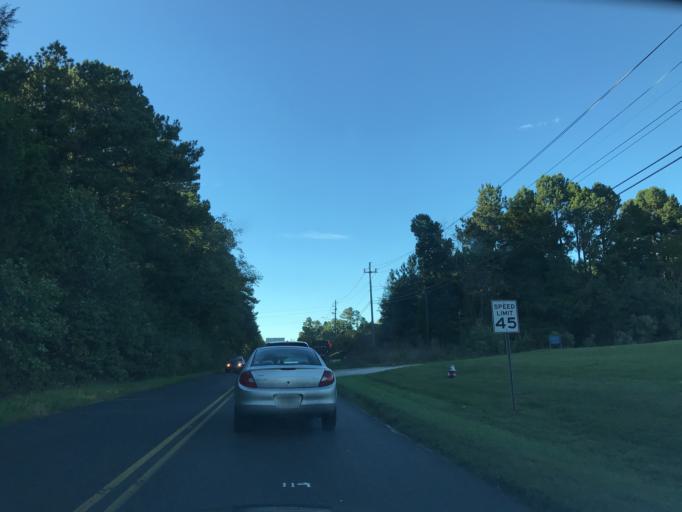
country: US
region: North Carolina
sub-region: Wake County
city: Morrisville
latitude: 35.8410
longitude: -78.8326
